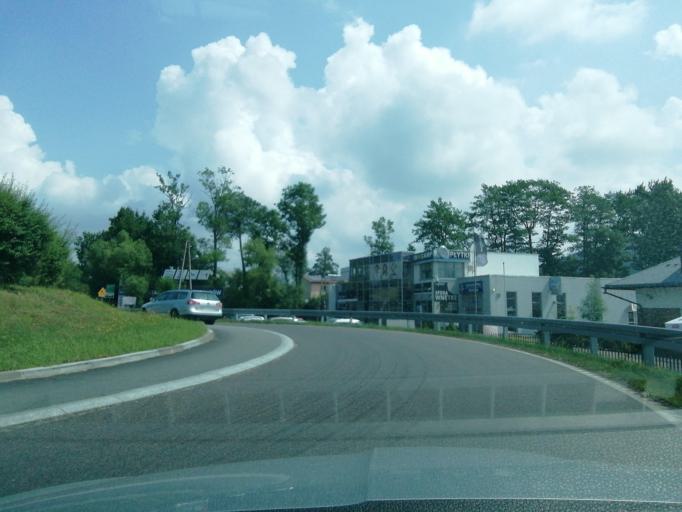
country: PL
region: Silesian Voivodeship
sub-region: Powiat zywiecki
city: Wieprz
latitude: 49.6583
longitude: 19.1719
